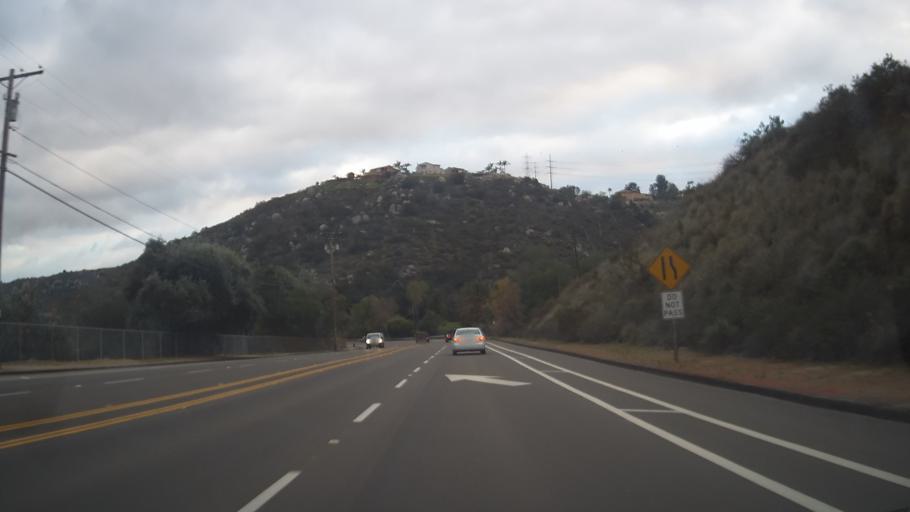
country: US
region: California
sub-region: San Diego County
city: Granite Hills
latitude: 32.7856
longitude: -116.8889
